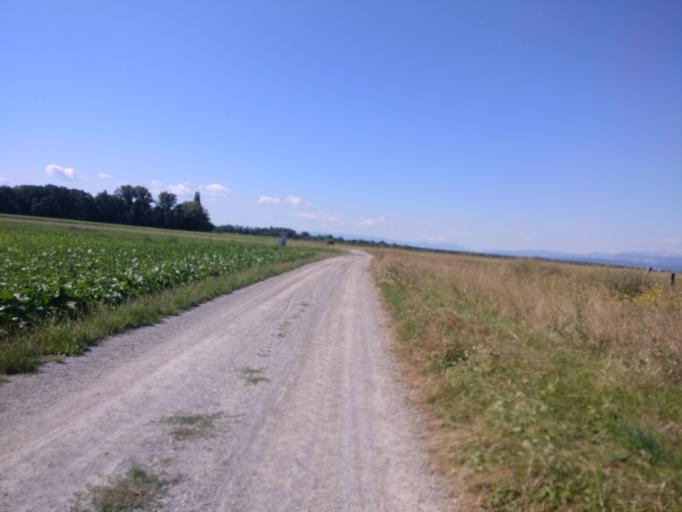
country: AT
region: Lower Austria
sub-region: Politischer Bezirk Baden
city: Pottendorf
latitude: 47.9159
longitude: 16.3572
